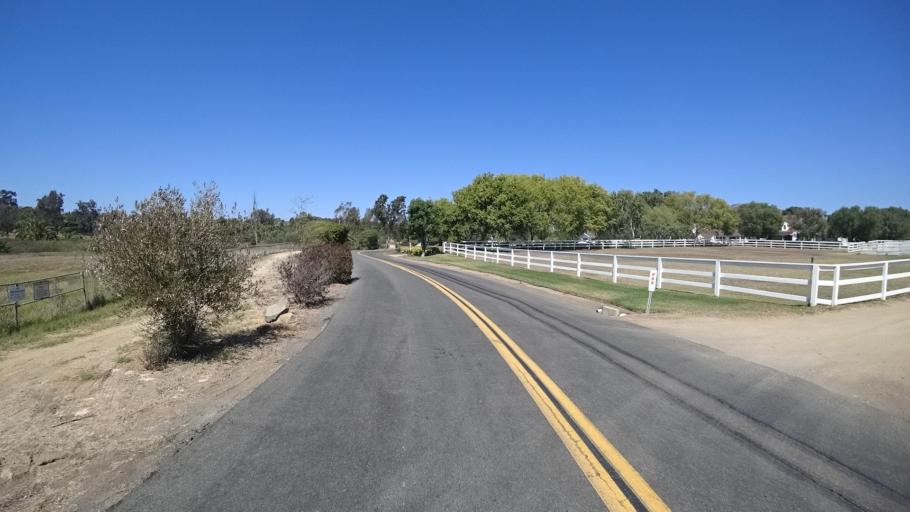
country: US
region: California
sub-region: San Diego County
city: Rancho Santa Fe
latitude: 33.0419
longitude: -117.1894
